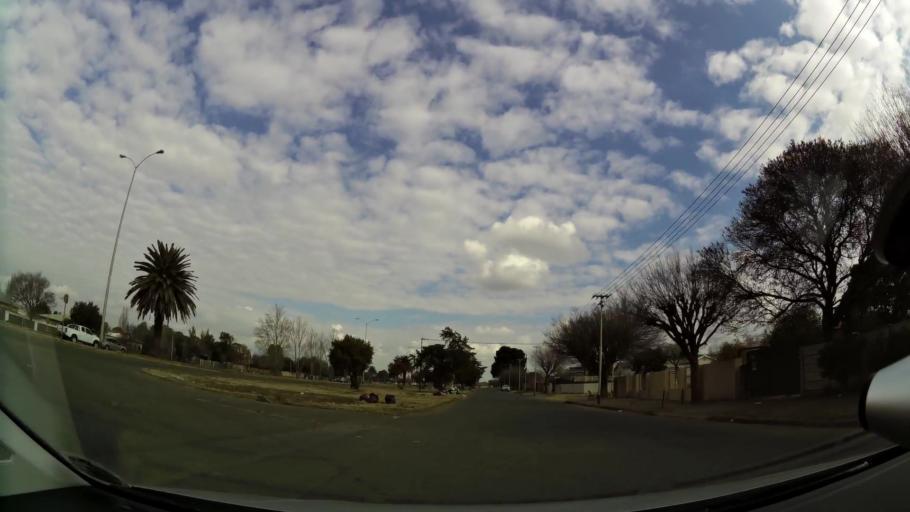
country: ZA
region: Orange Free State
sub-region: Mangaung Metropolitan Municipality
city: Bloemfontein
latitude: -29.0869
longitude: 26.2549
